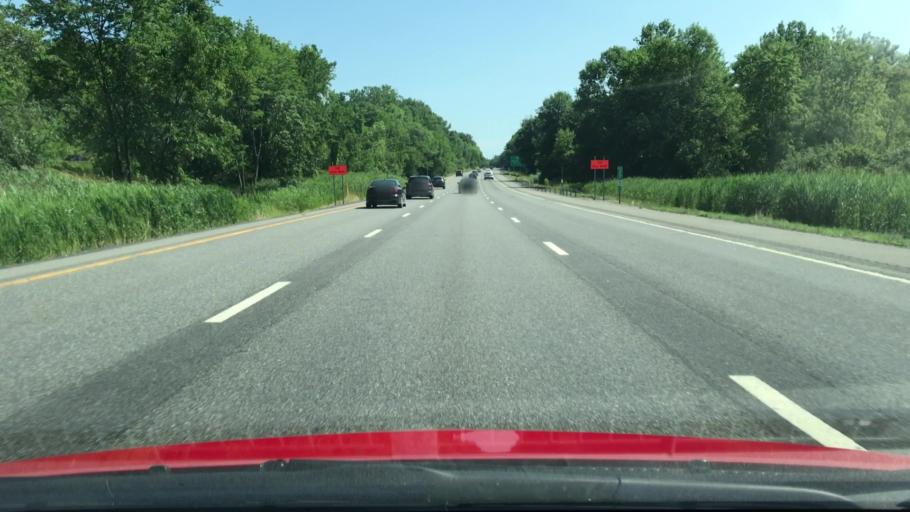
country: US
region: New York
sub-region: Saratoga County
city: Saratoga Springs
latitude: 43.0561
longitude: -73.7641
